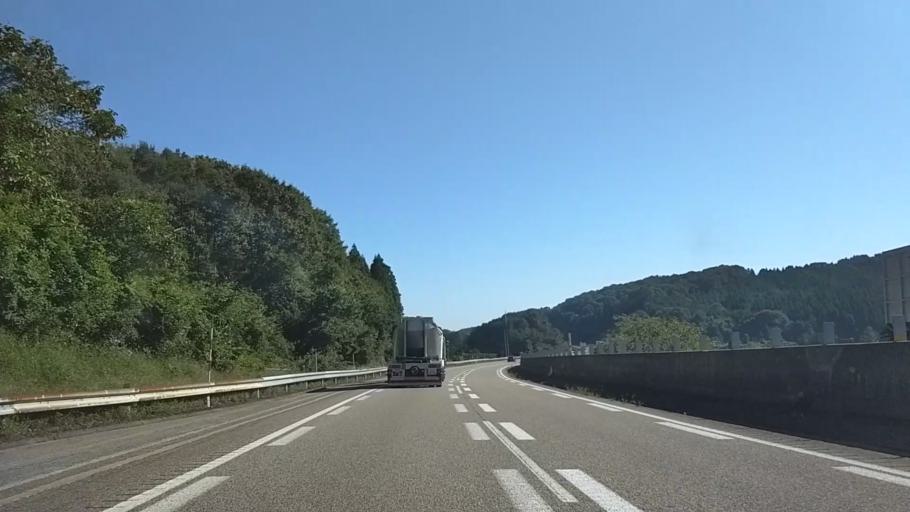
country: JP
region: Toyama
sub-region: Oyabe Shi
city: Oyabe
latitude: 36.6066
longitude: 136.8037
